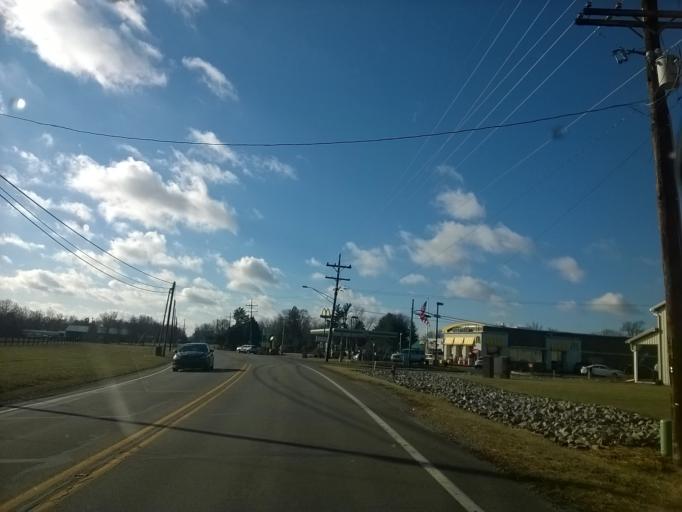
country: US
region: Indiana
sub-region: Jefferson County
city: Hanover
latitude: 38.7241
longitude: -85.4673
